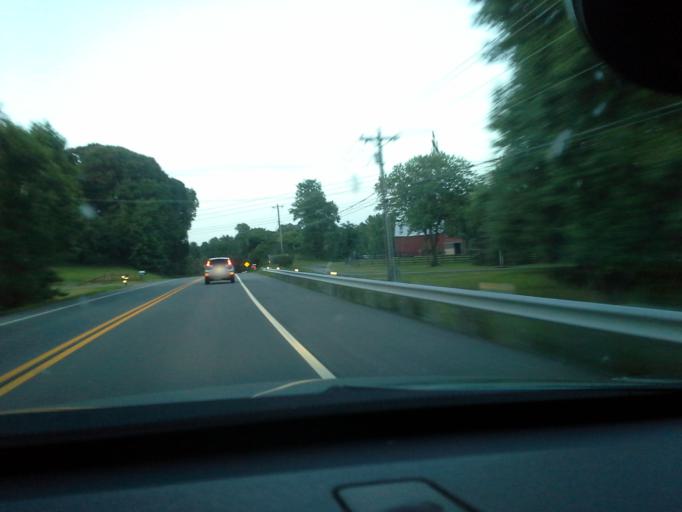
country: US
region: Maryland
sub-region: Calvert County
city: Huntingtown
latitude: 38.6108
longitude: -76.5648
